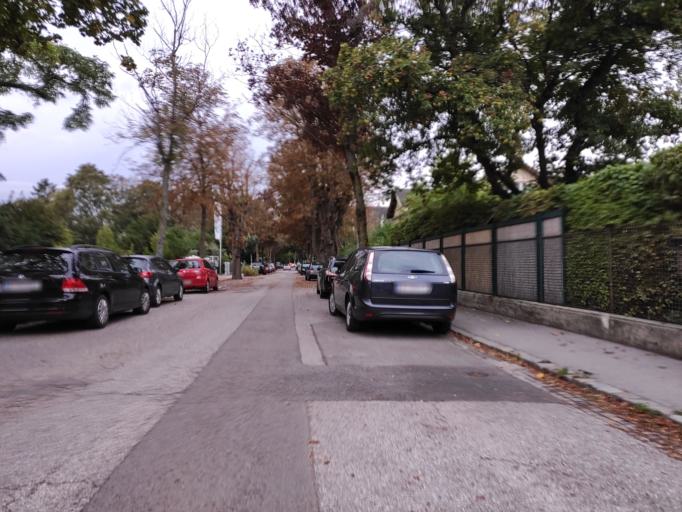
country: AT
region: Lower Austria
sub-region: Politischer Bezirk Baden
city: Baden
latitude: 48.0045
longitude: 16.2283
